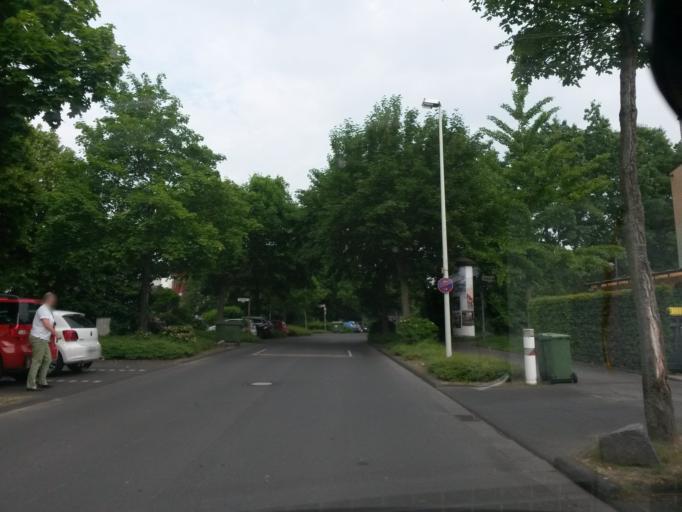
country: DE
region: North Rhine-Westphalia
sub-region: Regierungsbezirk Koln
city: Bonn
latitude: 50.7023
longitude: 7.0566
